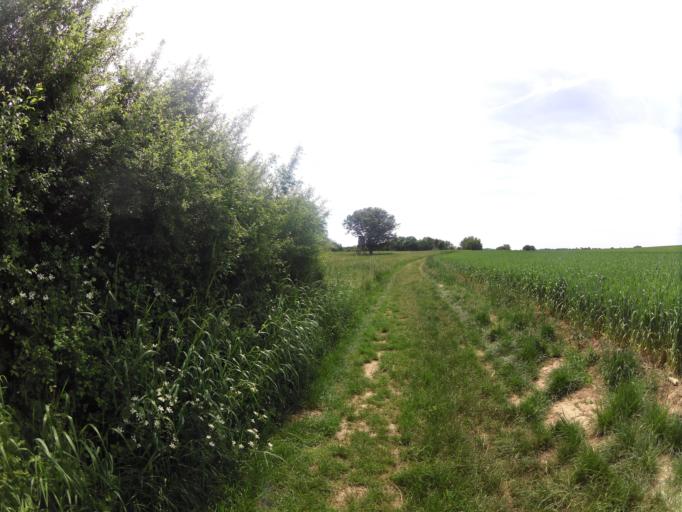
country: DE
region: Bavaria
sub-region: Regierungsbezirk Unterfranken
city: Ochsenfurt
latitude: 49.6585
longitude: 10.0282
